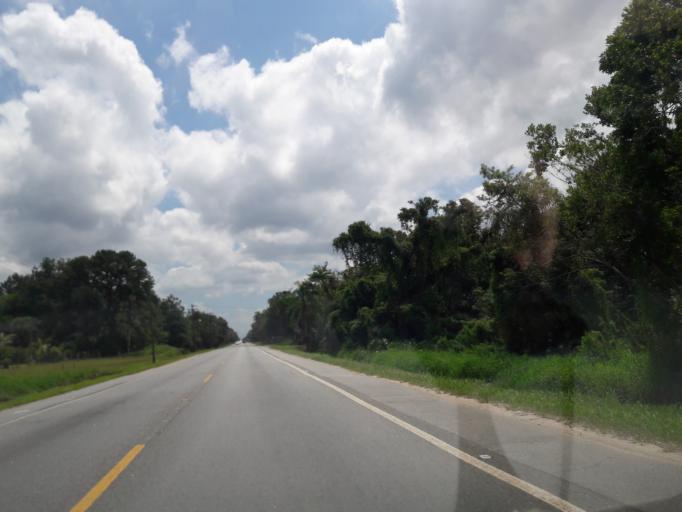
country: BR
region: Parana
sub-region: Pontal Do Parana
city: Pontal do Parana
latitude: -25.6395
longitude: -48.5340
